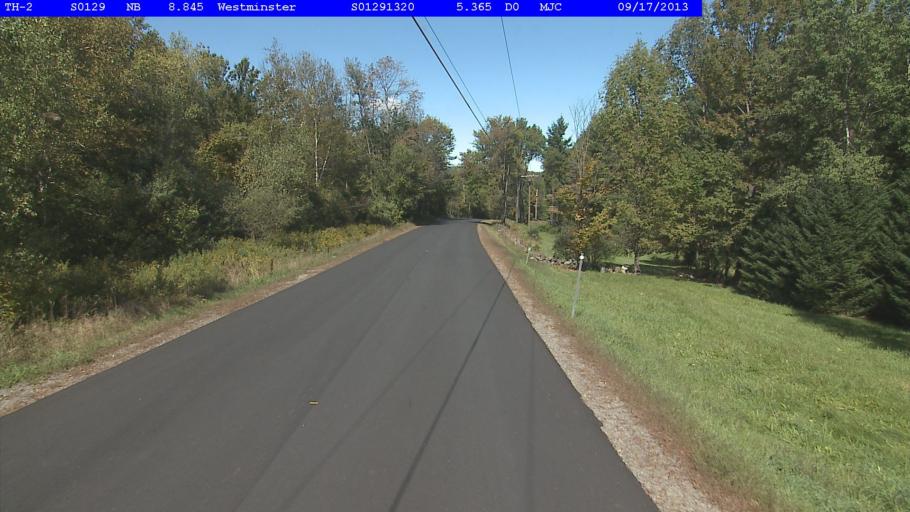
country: US
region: Vermont
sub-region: Windham County
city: Bellows Falls
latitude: 43.0923
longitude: -72.5355
